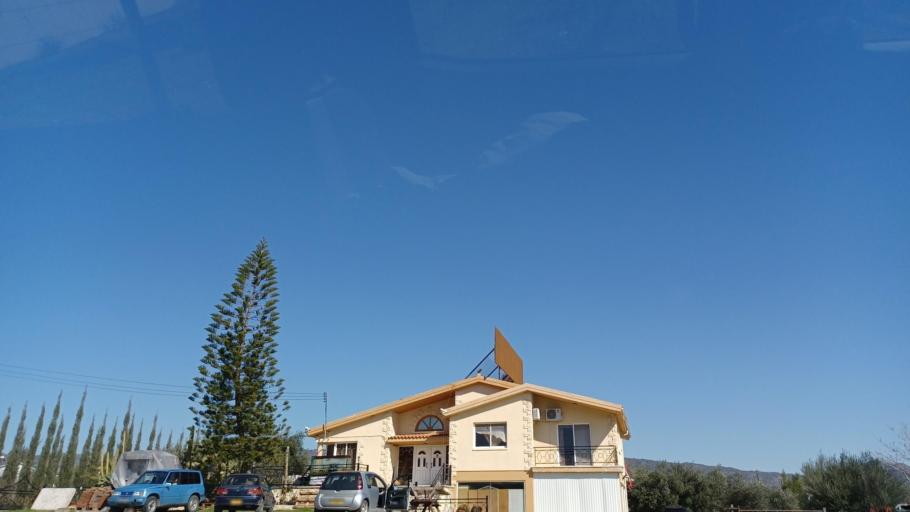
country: CY
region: Limassol
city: Parekklisha
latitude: 34.7484
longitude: 33.1556
